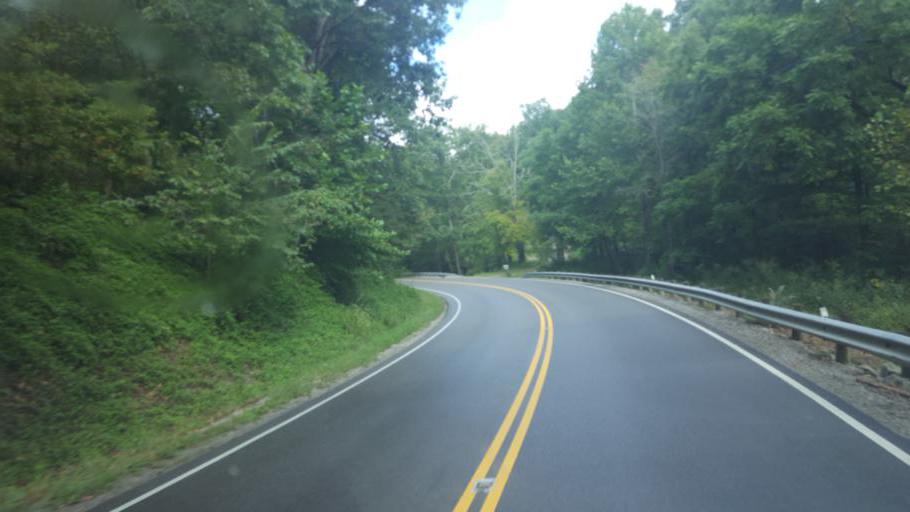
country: US
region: Ohio
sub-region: Scioto County
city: Sciotodale
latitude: 38.8779
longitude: -82.7988
